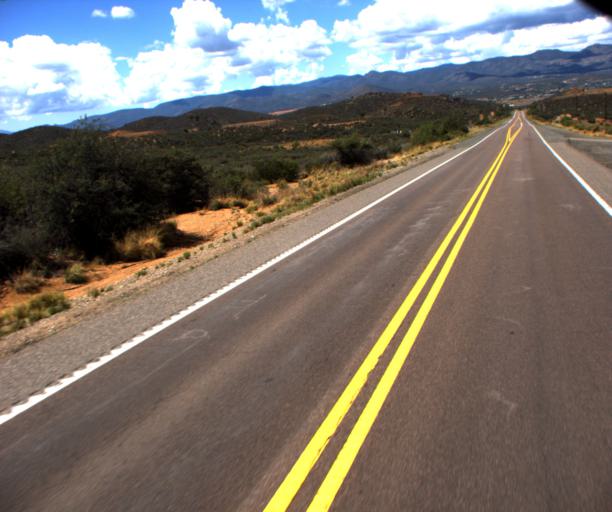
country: US
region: Arizona
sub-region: Yavapai County
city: Dewey-Humboldt
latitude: 34.5422
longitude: -112.1913
